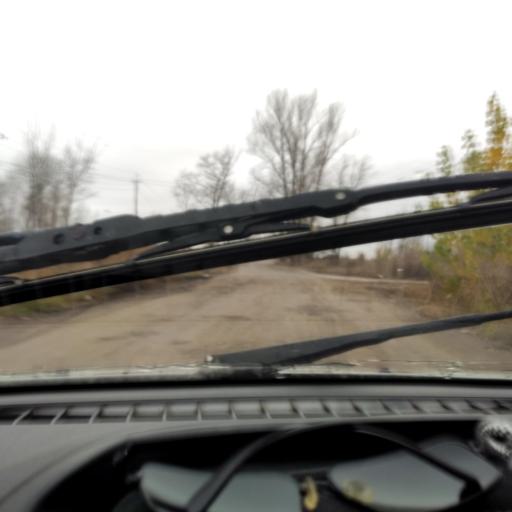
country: RU
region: Samara
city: Tol'yatti
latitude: 53.5441
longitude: 49.3950
